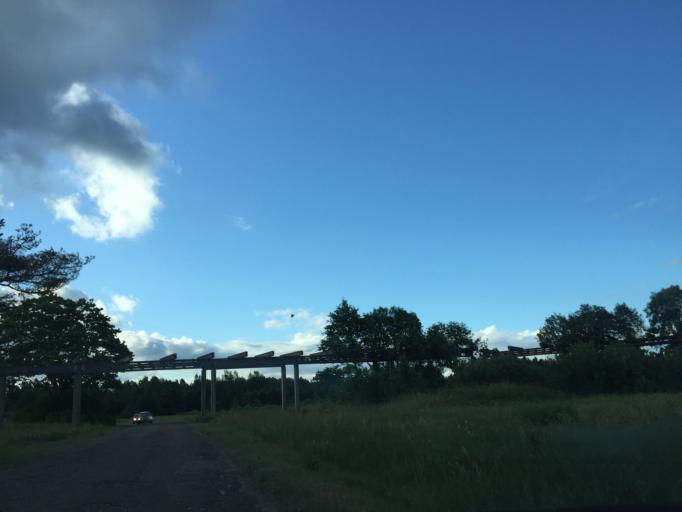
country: LV
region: Ventspils
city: Ventspils
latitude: 57.4103
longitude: 21.6169
